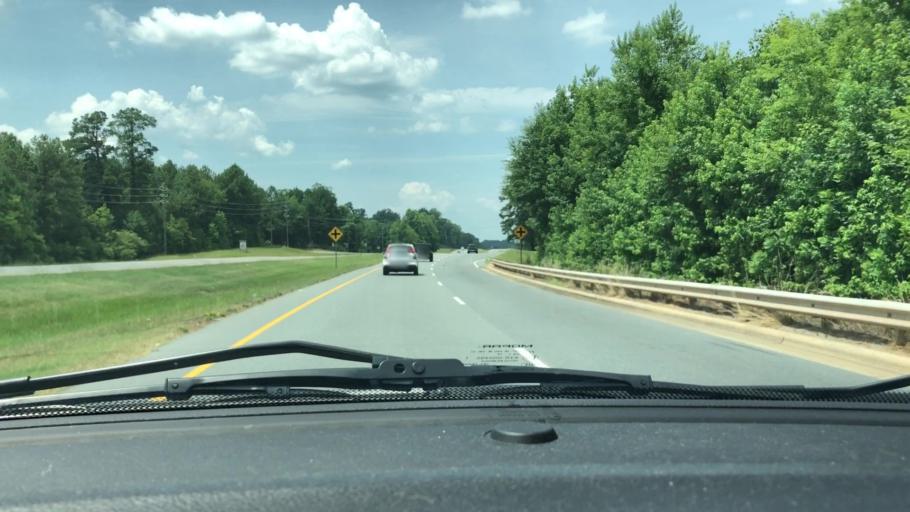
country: US
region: North Carolina
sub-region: Lee County
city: Sanford
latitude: 35.5021
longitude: -79.2052
